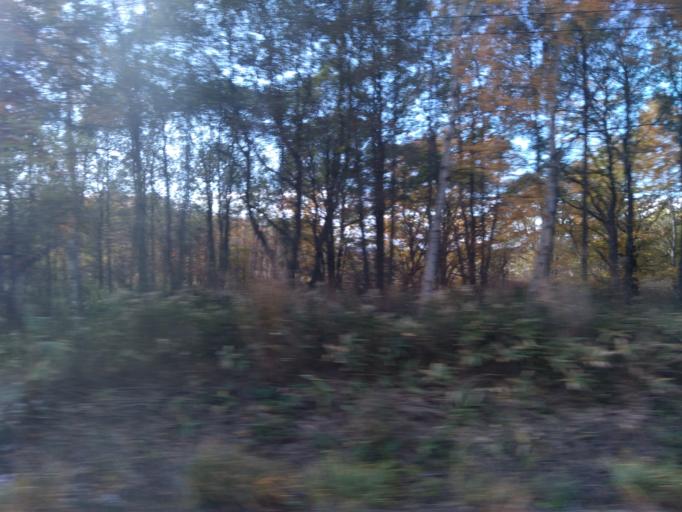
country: JP
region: Hokkaido
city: Kitahiroshima
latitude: 42.9113
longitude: 141.5739
